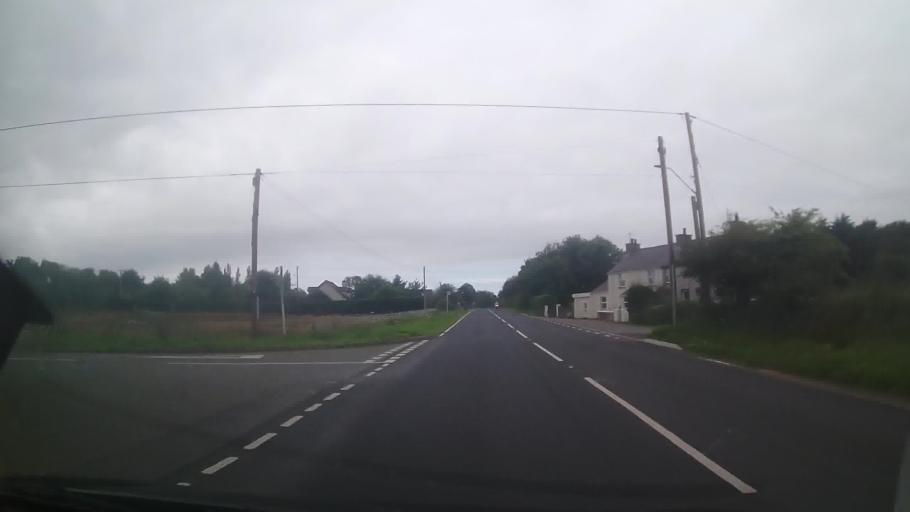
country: GB
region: Wales
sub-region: Gwynedd
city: Caernarfon
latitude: 53.1636
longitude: -4.3178
